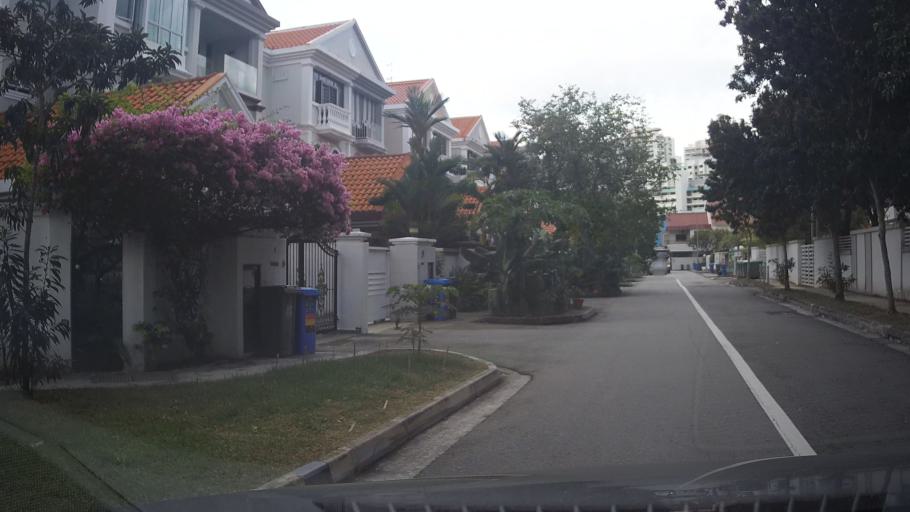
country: SG
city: Singapore
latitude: 1.3084
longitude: 103.9141
